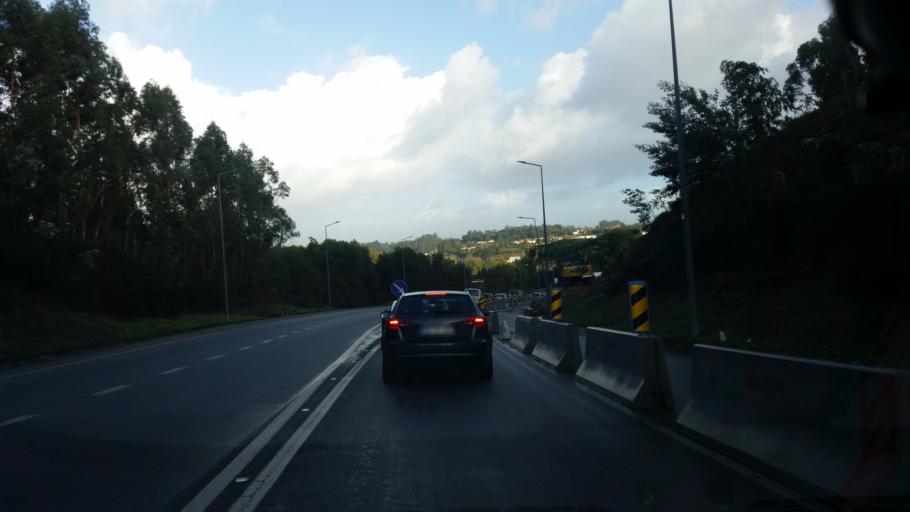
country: PT
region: Porto
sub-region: Santo Tirso
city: Santo Tirso
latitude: 41.3405
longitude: -8.4675
